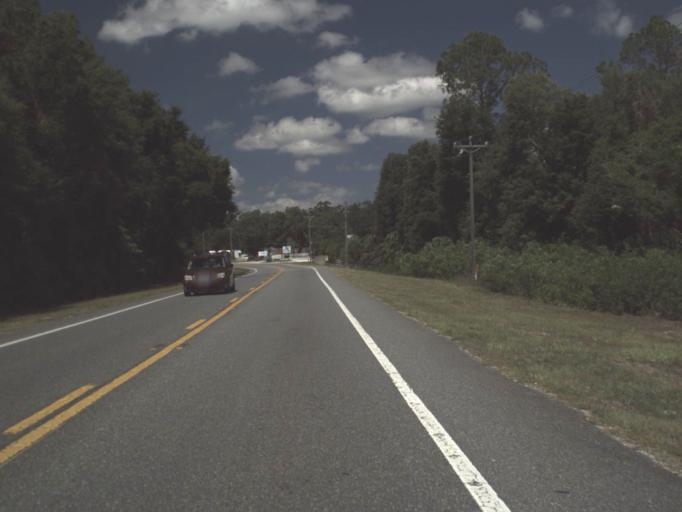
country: US
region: Florida
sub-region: Marion County
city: Silver Springs Shores
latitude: 29.1762
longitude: -81.8352
